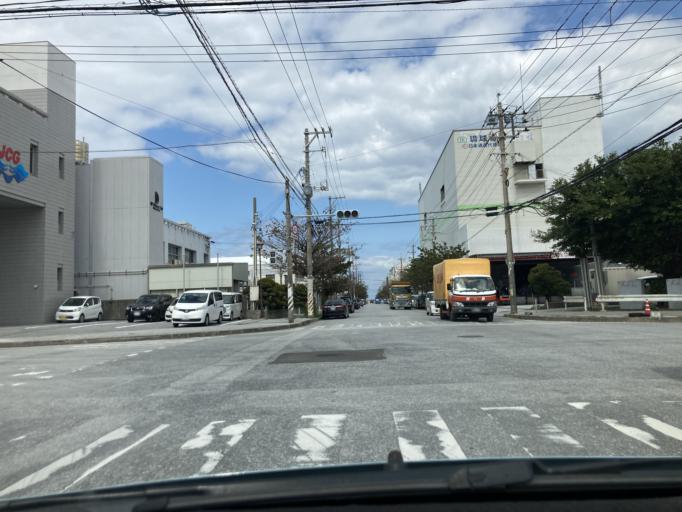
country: JP
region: Okinawa
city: Naha-shi
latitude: 26.2458
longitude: 127.6732
